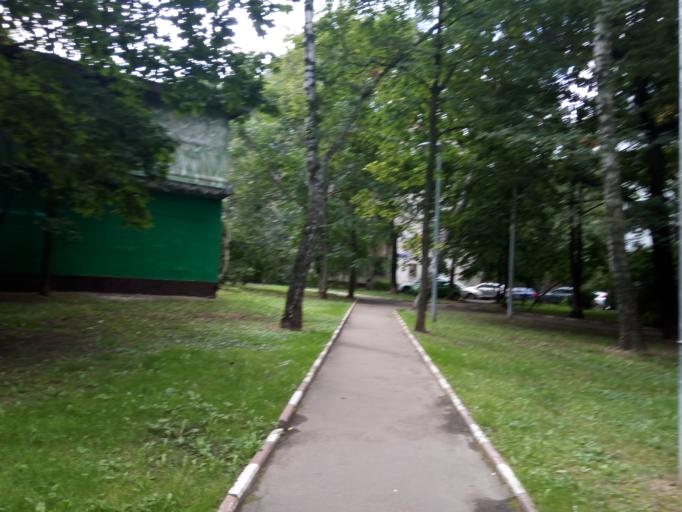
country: RU
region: Moscow
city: Sokol
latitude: 55.7825
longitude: 37.5184
